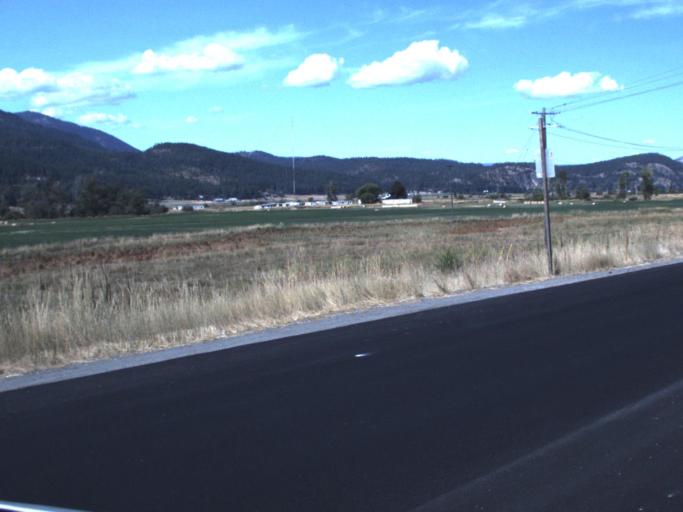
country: US
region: Washington
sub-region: Stevens County
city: Colville
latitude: 48.5173
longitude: -117.9006
